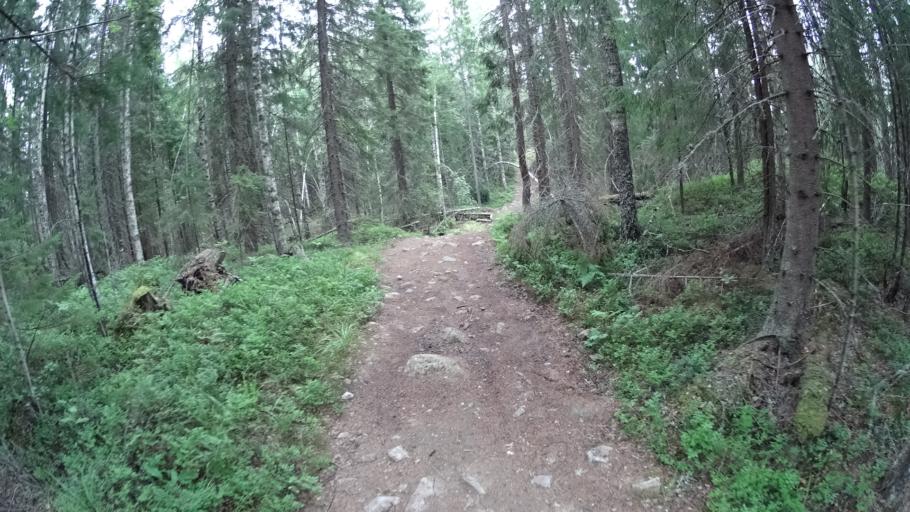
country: FI
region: Southern Savonia
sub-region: Mikkeli
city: Maentyharju
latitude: 61.1815
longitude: 26.8888
